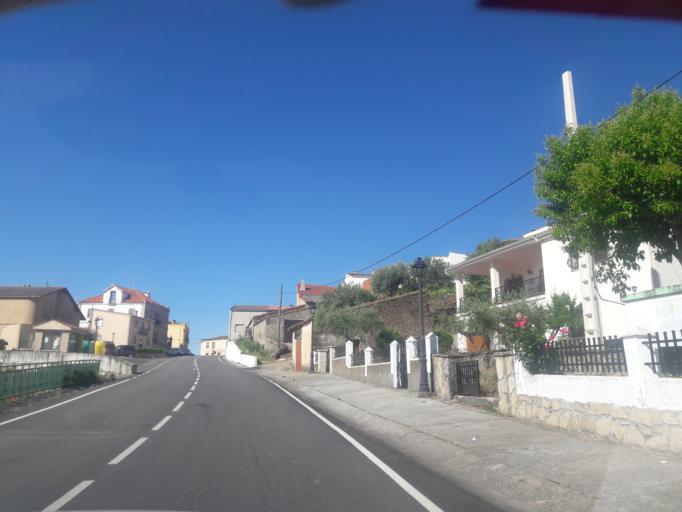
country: ES
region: Castille and Leon
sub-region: Provincia de Salamanca
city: Saucelle
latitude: 41.0470
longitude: -6.7521
